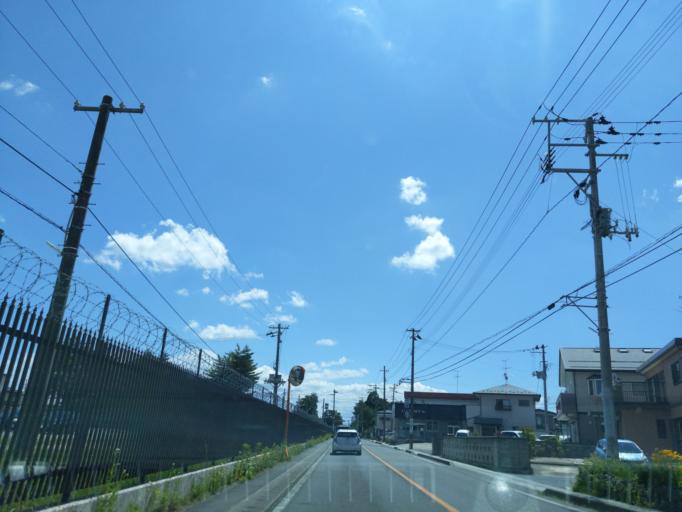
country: JP
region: Fukushima
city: Koriyama
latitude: 37.3978
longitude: 140.3228
